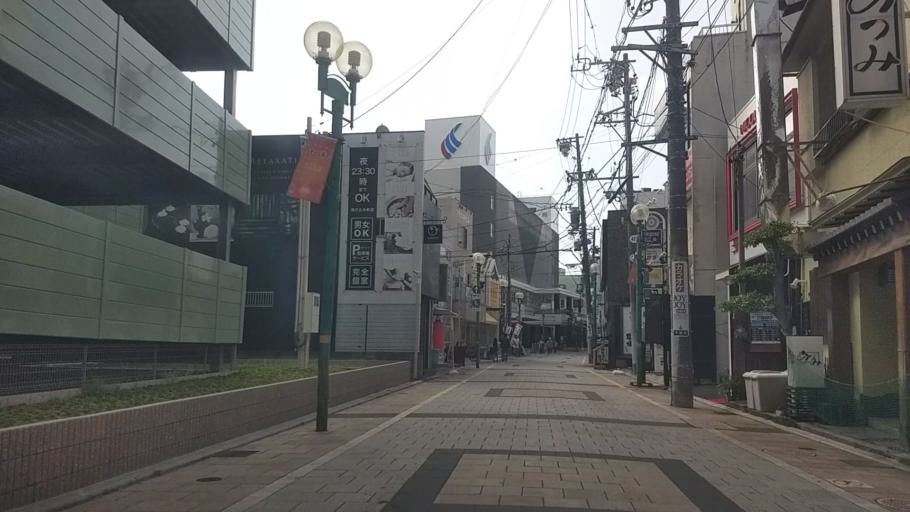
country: JP
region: Shizuoka
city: Hamamatsu
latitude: 34.7046
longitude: 137.7309
